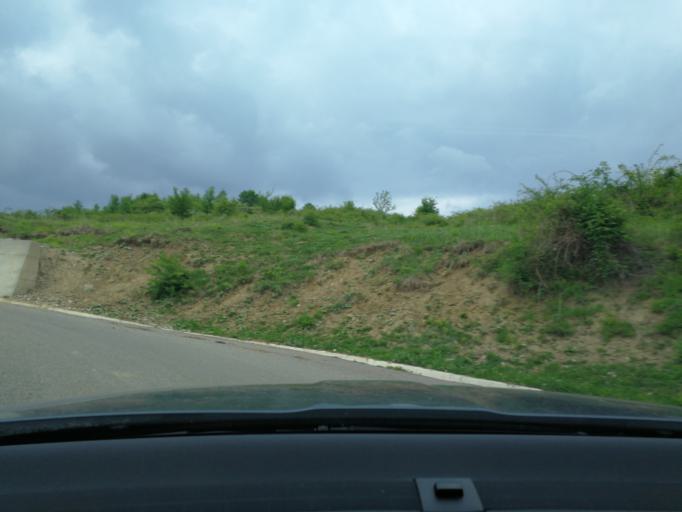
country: RO
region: Prahova
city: Cornu de Sus
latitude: 45.1701
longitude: 25.7073
